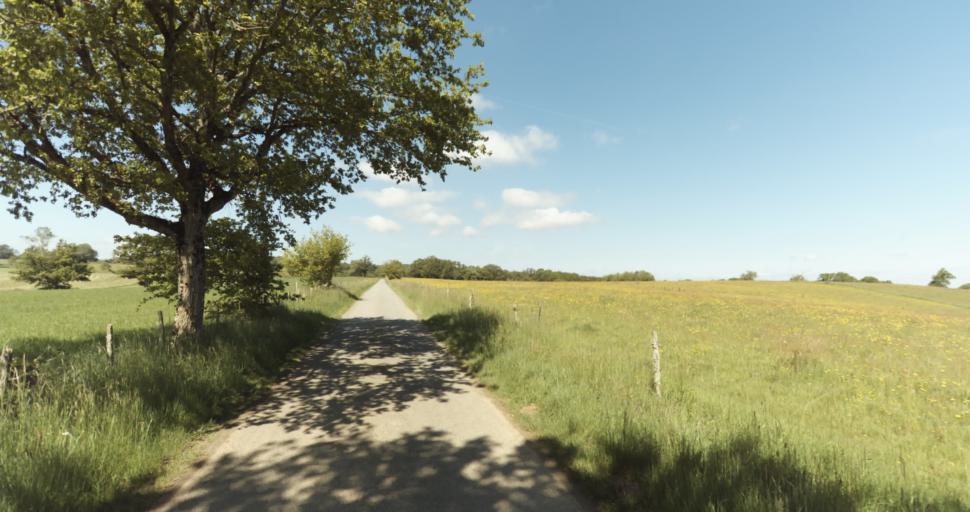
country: FR
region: Limousin
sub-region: Departement de la Haute-Vienne
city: Le Vigen
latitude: 45.7219
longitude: 1.2921
